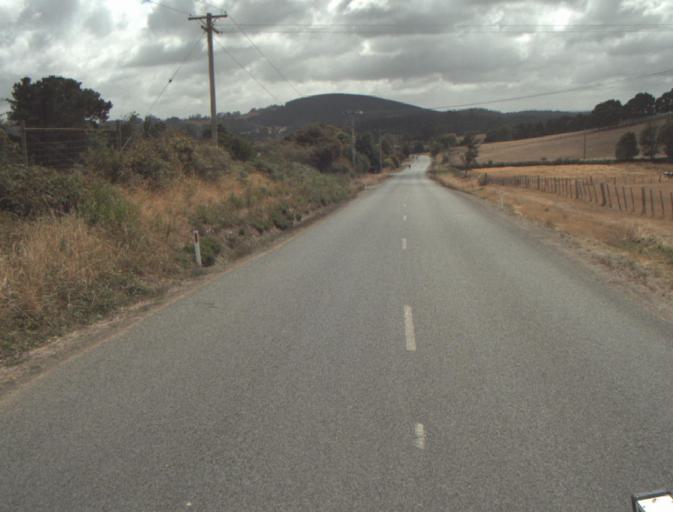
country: AU
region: Tasmania
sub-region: Launceston
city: Mayfield
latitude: -41.1993
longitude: 147.2176
